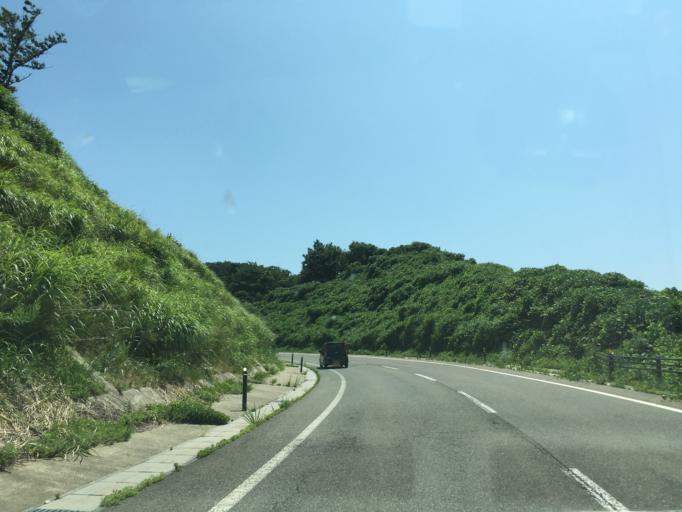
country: JP
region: Akita
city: Tenno
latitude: 39.9573
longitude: 139.7215
